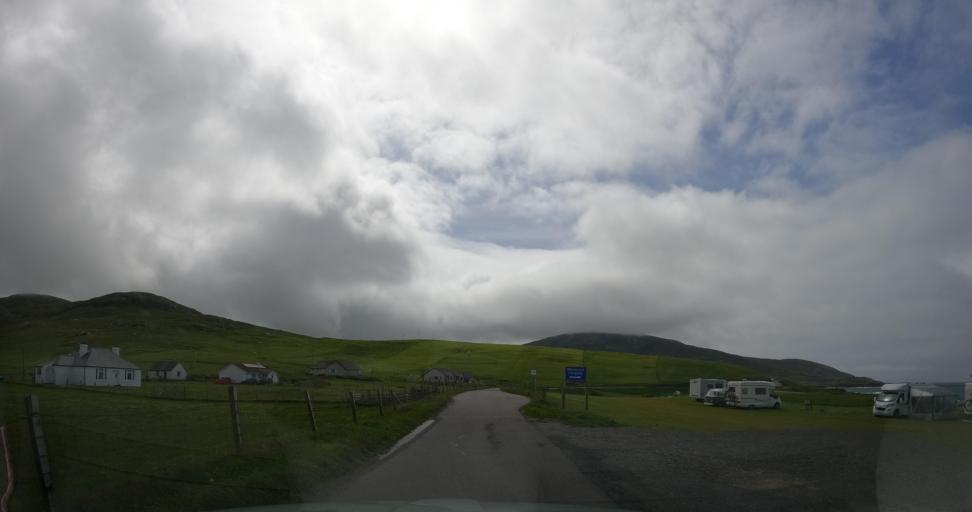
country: GB
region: Scotland
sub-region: Eilean Siar
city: Barra
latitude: 56.9804
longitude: -7.5117
